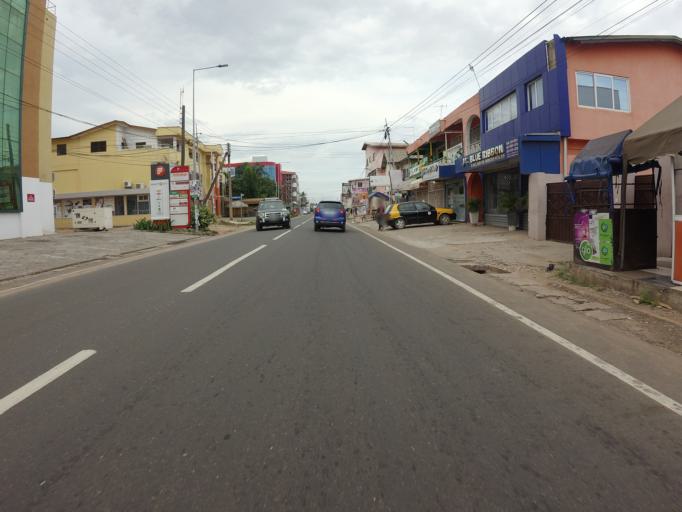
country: GH
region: Greater Accra
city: Dome
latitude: 5.6106
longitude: -0.2045
